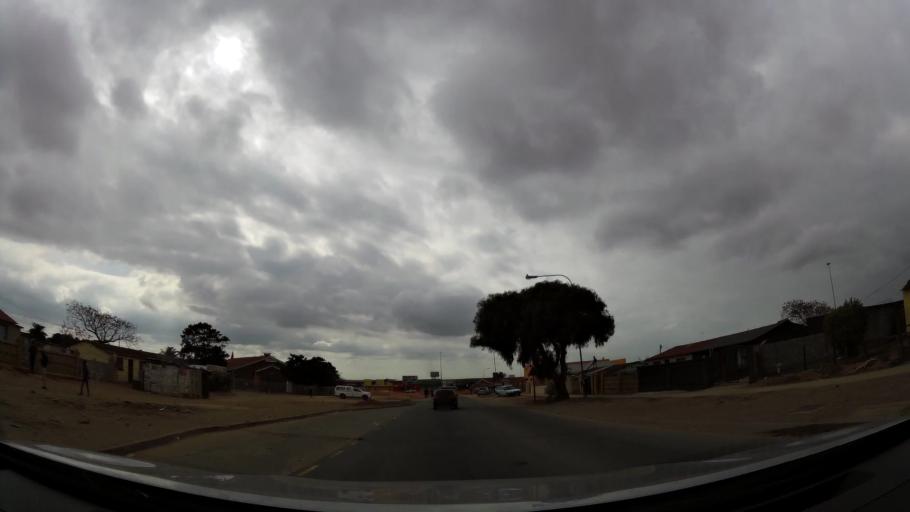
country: ZA
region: Eastern Cape
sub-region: Nelson Mandela Bay Metropolitan Municipality
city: Port Elizabeth
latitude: -33.8722
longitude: 25.5647
